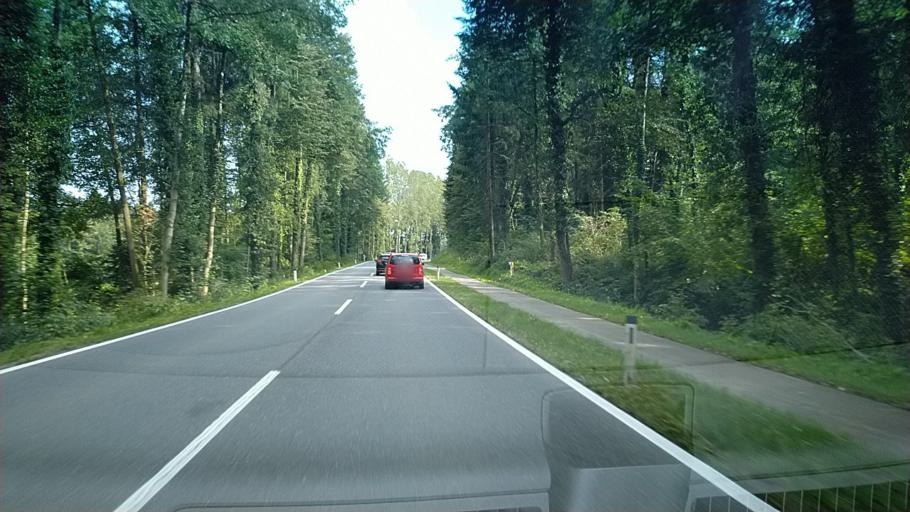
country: AT
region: Styria
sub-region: Politischer Bezirk Deutschlandsberg
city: Hollenegg
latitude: 46.7885
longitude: 15.2278
